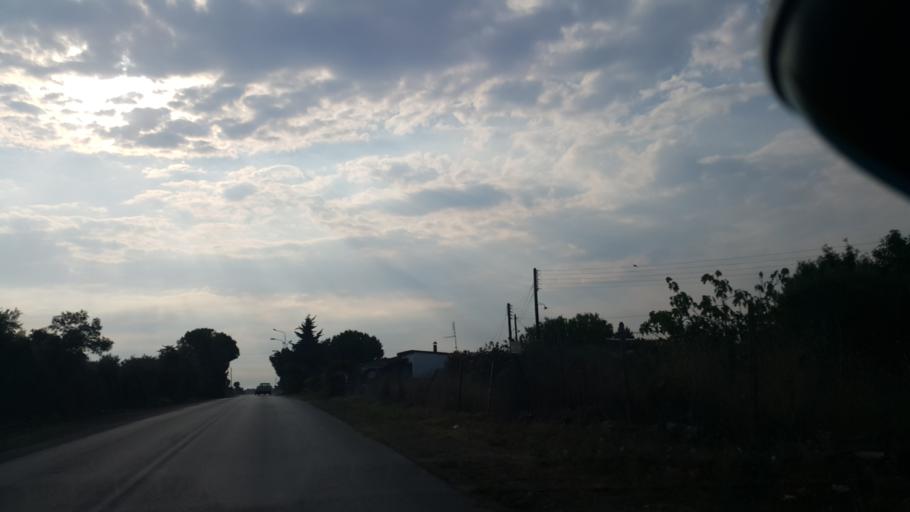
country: GR
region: Central Macedonia
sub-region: Nomos Chalkidikis
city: Nea Kallikrateia
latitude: 40.3175
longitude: 23.0764
